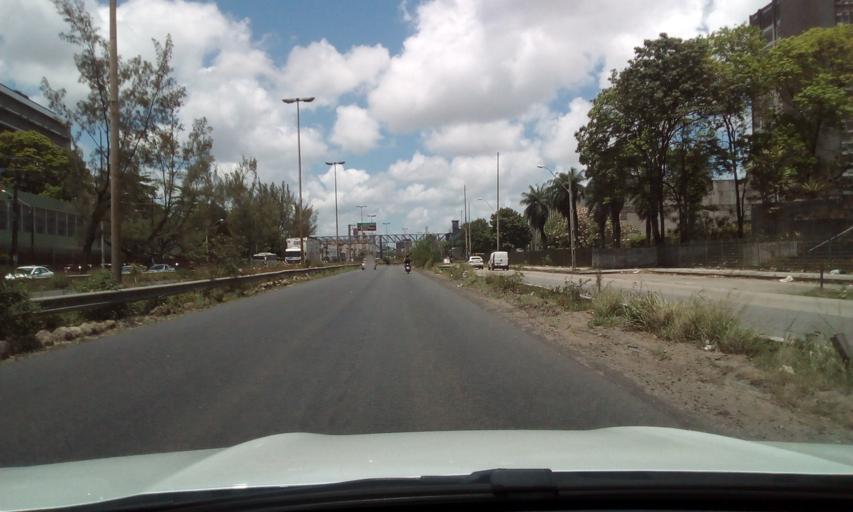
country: BR
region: Pernambuco
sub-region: Recife
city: Recife
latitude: -8.0488
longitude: -34.9454
